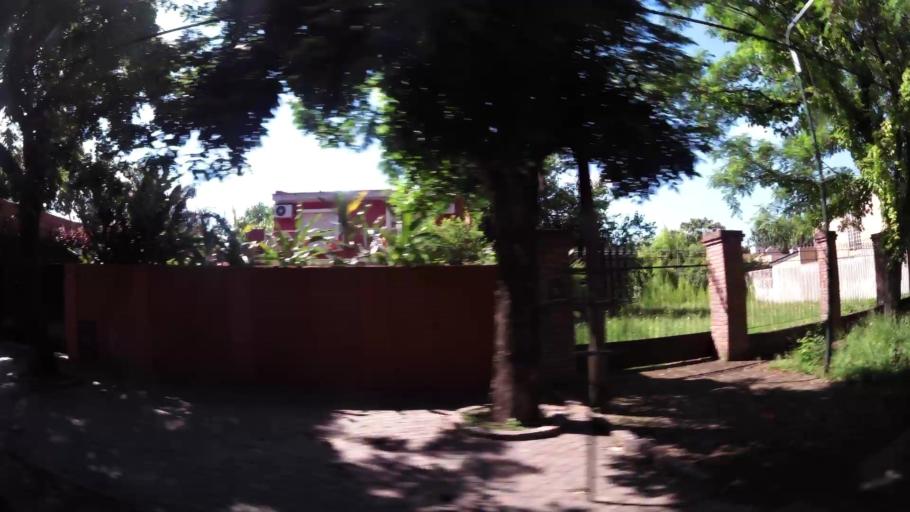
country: AR
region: Buenos Aires
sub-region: Partido de Tigre
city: Tigre
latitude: -34.4842
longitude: -58.5757
